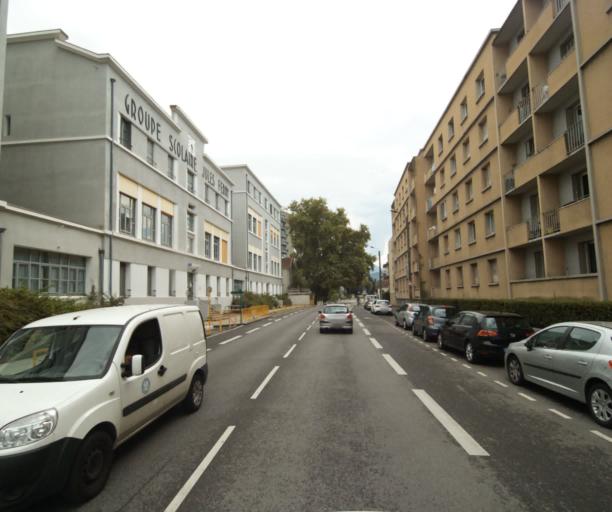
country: FR
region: Rhone-Alpes
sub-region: Departement de l'Isere
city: La Tronche
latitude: 45.1804
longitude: 5.7417
